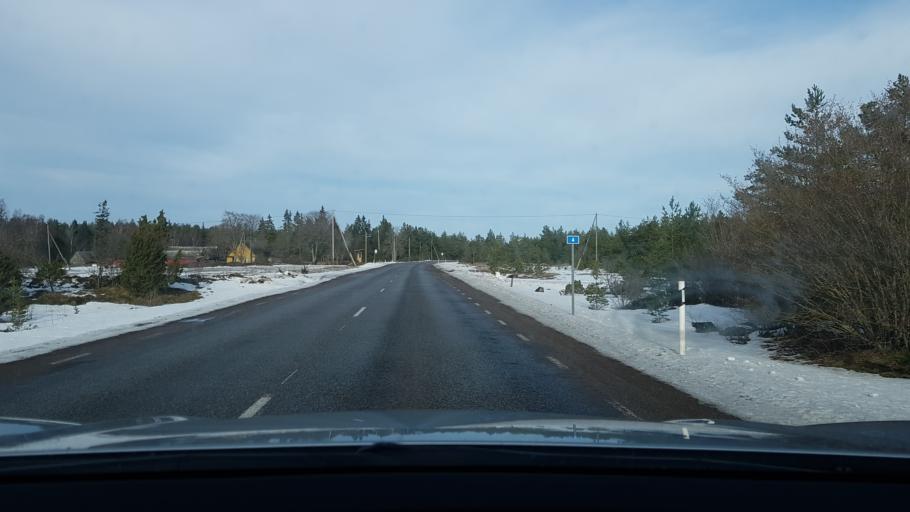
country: EE
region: Saare
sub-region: Kuressaare linn
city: Kuressaare
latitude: 58.3167
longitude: 22.5455
